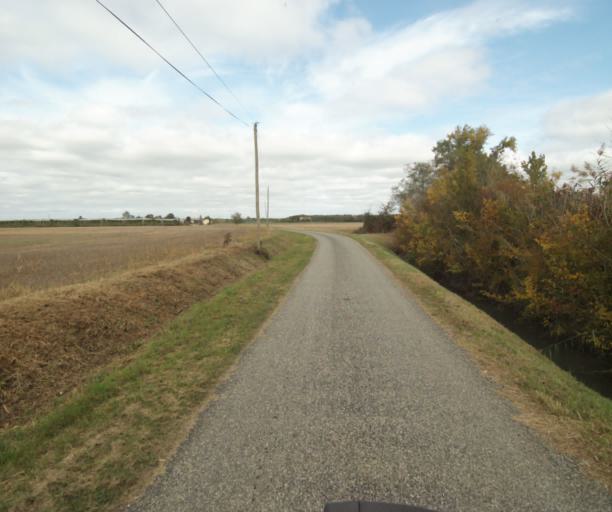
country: FR
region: Midi-Pyrenees
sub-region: Departement du Tarn-et-Garonne
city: Finhan
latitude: 43.9301
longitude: 1.2059
